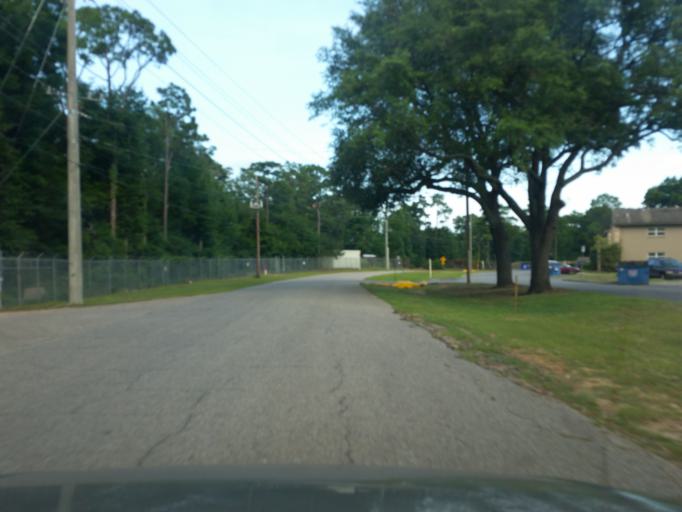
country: US
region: Florida
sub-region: Escambia County
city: Ferry Pass
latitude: 30.5157
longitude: -87.1719
